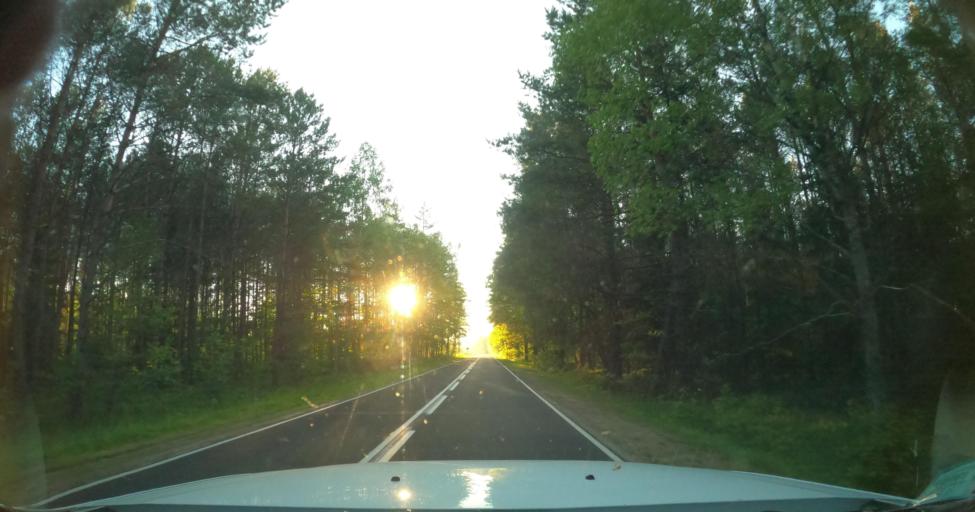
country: PL
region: Pomeranian Voivodeship
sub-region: Powiat slupski
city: Potegowo
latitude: 54.3980
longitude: 17.4659
